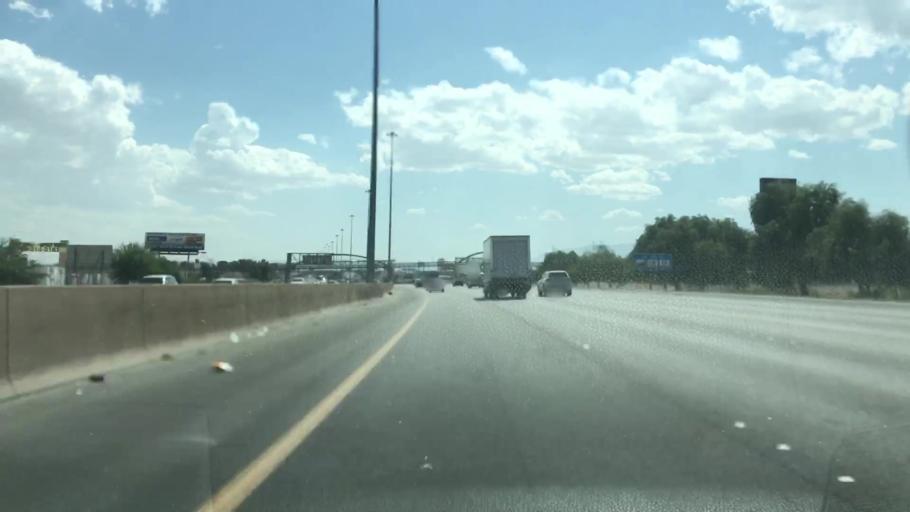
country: US
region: Nevada
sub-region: Clark County
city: North Las Vegas
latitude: 36.2291
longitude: -115.1159
